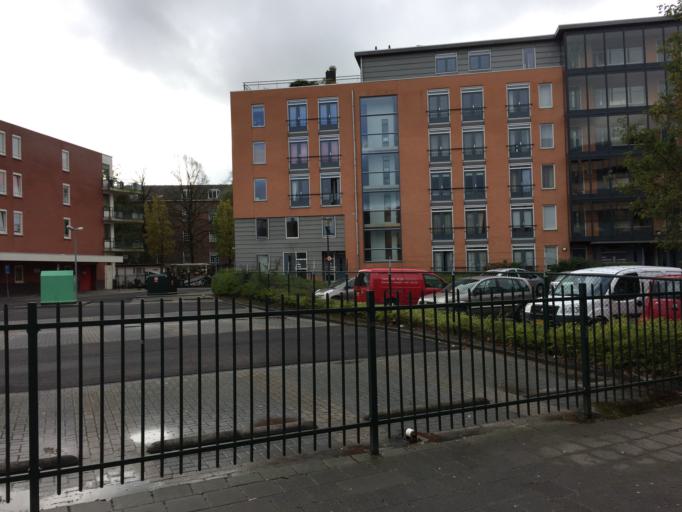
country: NL
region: Friesland
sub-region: Gemeente Leeuwarden
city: Leeuwarden
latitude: 53.2060
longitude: 5.8043
